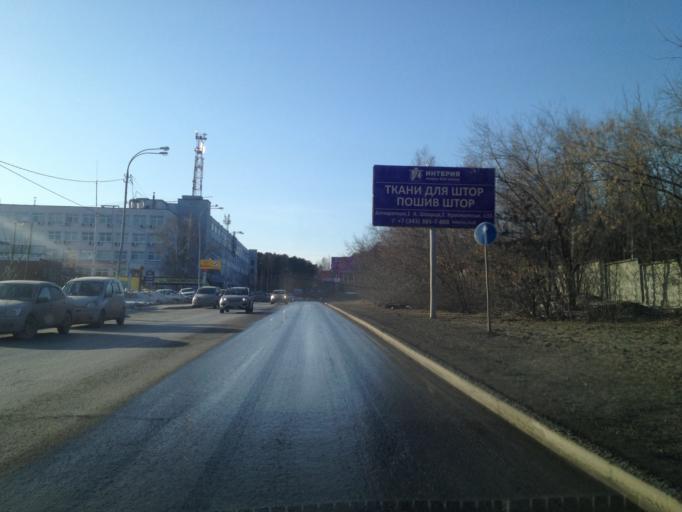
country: RU
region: Sverdlovsk
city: Sovkhoznyy
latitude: 56.8128
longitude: 60.5394
